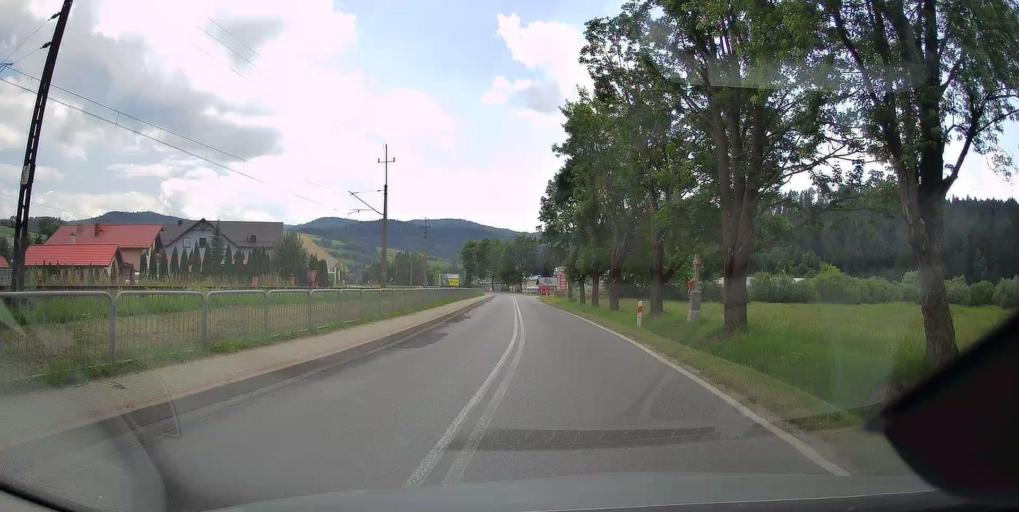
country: PL
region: Lesser Poland Voivodeship
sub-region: Powiat nowosadecki
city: Krynica-Zdroj
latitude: 49.3792
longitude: 20.9514
